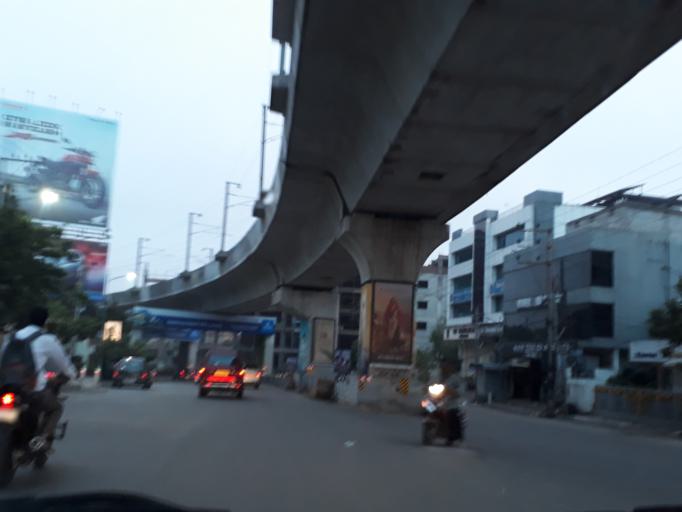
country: IN
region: Telangana
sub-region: Rangareddi
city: Kukatpalli
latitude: 17.4295
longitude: 78.4125
